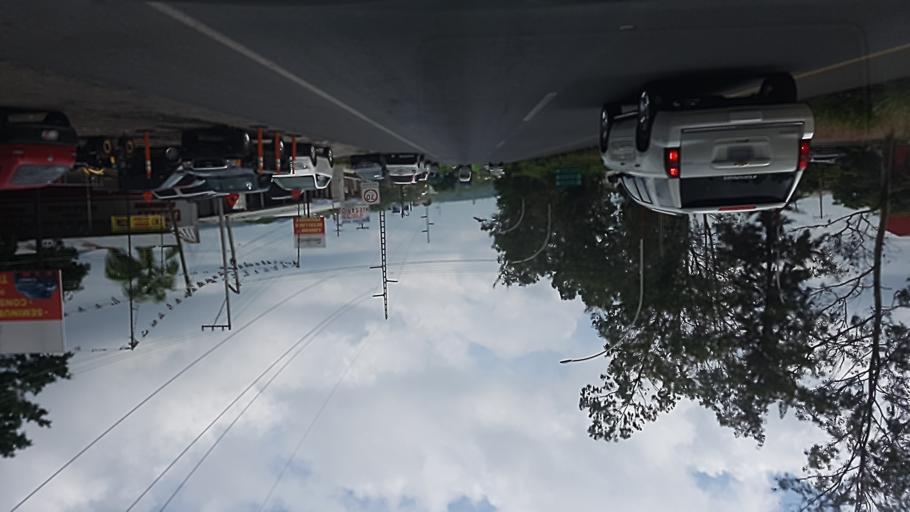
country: MX
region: Nayarit
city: Tepic
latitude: 21.5171
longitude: -104.9249
